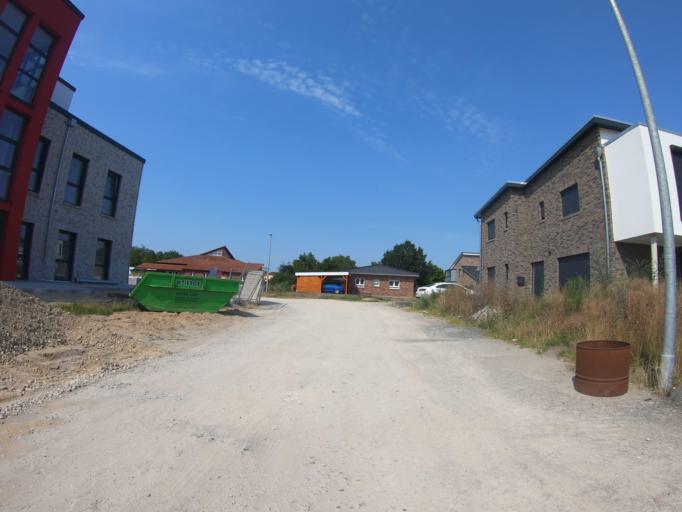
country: DE
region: Lower Saxony
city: Gifhorn
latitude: 52.4739
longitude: 10.5749
